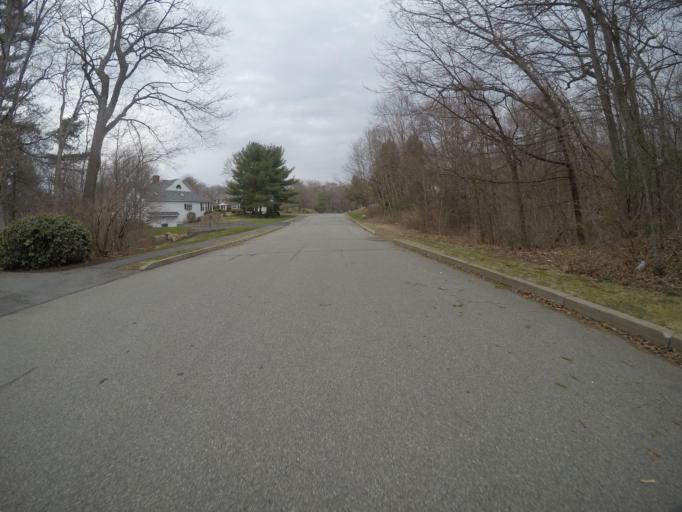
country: US
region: Massachusetts
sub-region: Norfolk County
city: Stoughton
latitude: 42.0813
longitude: -71.1034
